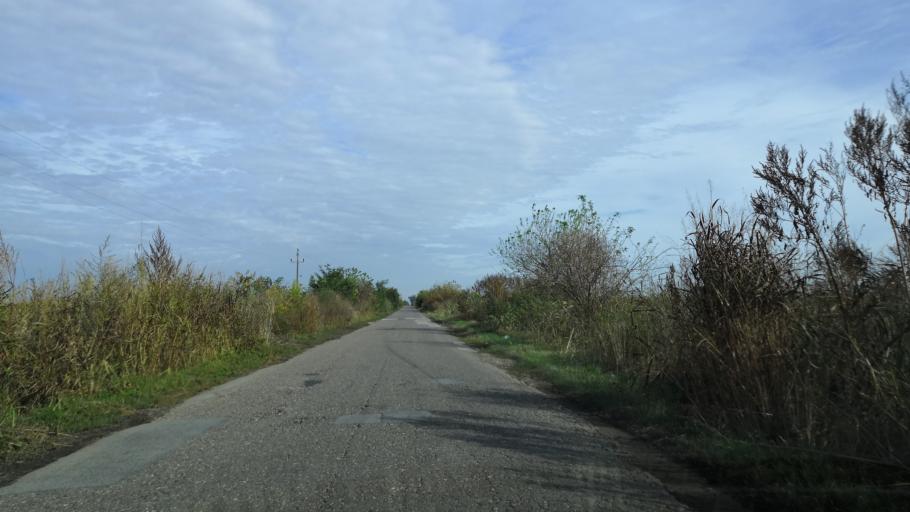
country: RS
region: Autonomna Pokrajina Vojvodina
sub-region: Sremski Okrug
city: Stara Pazova
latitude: 44.9994
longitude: 20.1648
